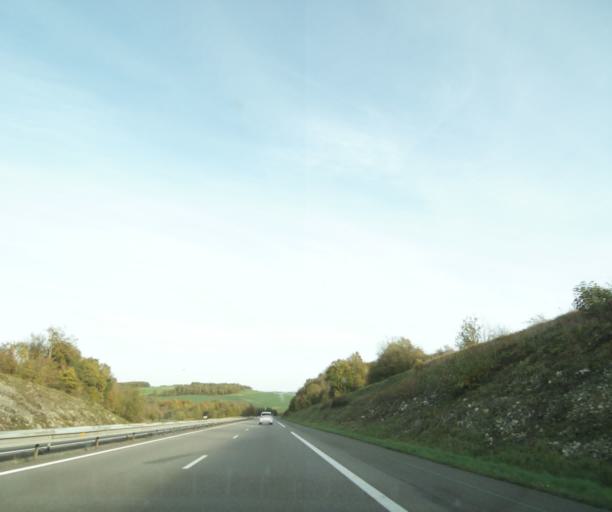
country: FR
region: Lorraine
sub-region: Departement de la Meuse
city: Clermont-en-Argonne
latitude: 49.0914
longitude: 5.2213
